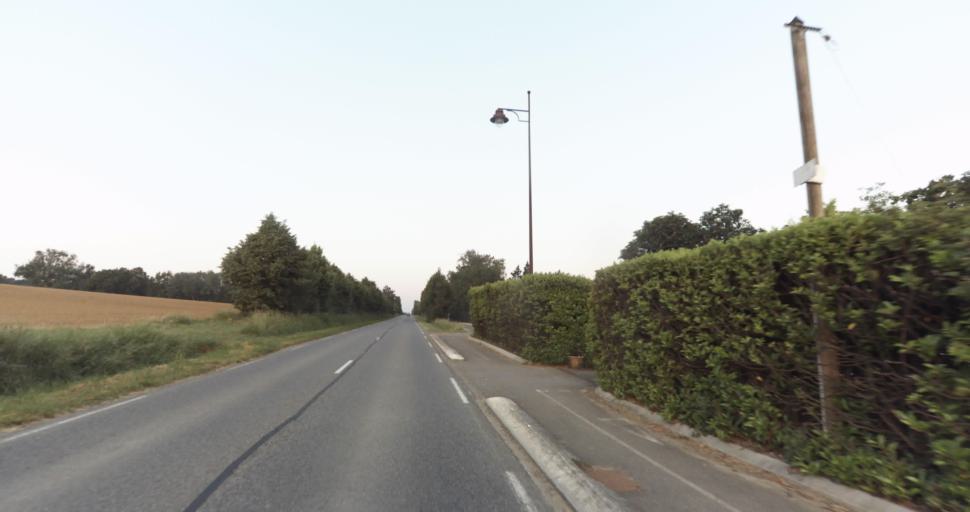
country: FR
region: Midi-Pyrenees
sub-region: Departement de la Haute-Garonne
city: Levignac
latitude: 43.6572
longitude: 1.1809
